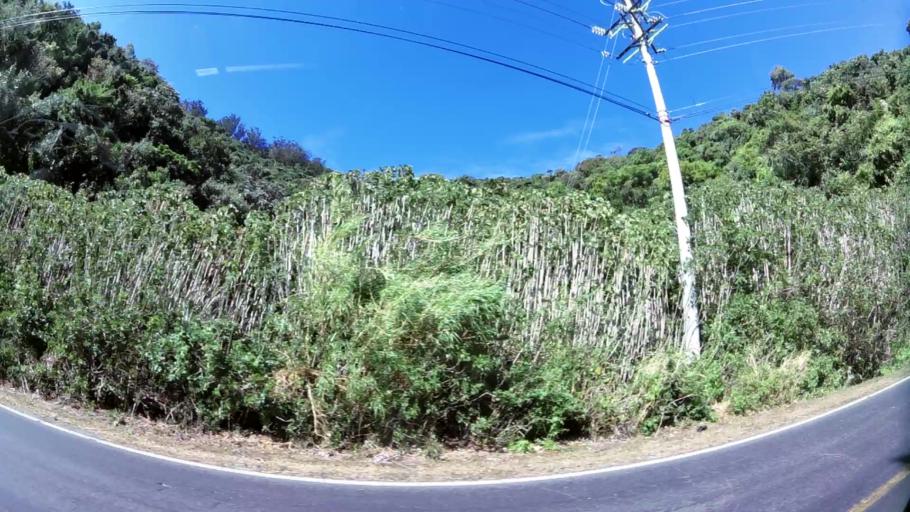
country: SV
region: Sonsonate
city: Juayua
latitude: 13.8489
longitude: -89.7676
